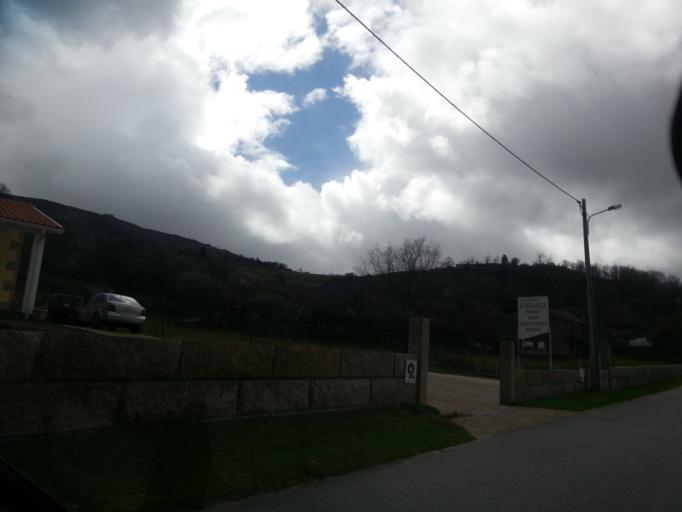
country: PT
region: Guarda
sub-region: Celorico da Beira
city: Celorico da Beira
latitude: 40.5458
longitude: -7.4565
